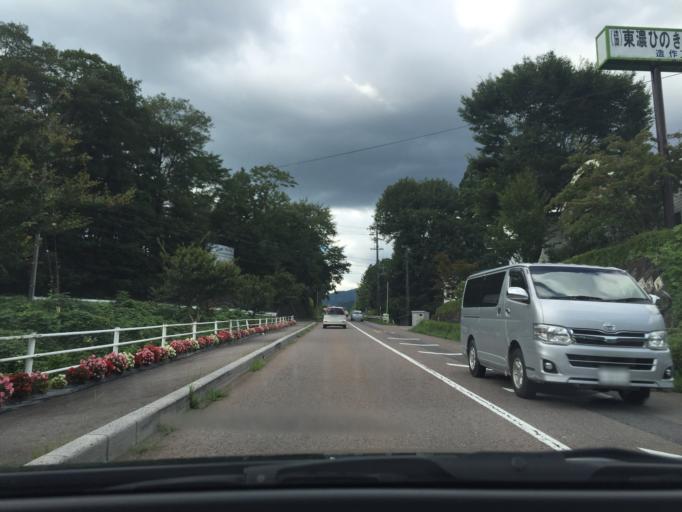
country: JP
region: Gifu
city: Nakatsugawa
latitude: 35.7368
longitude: 137.3433
